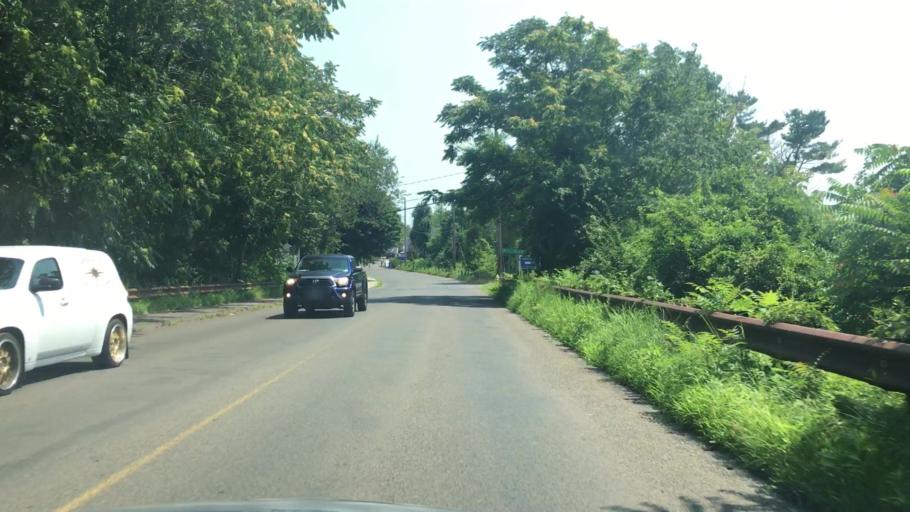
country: US
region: Connecticut
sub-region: New Haven County
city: Guilford Center
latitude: 41.2749
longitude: -72.6746
